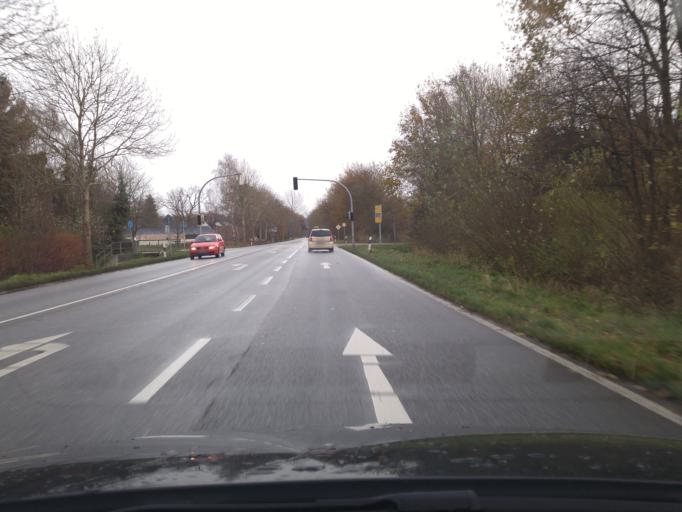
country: DE
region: Schleswig-Holstein
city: Timmendorfer Strand
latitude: 53.9891
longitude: 10.7913
